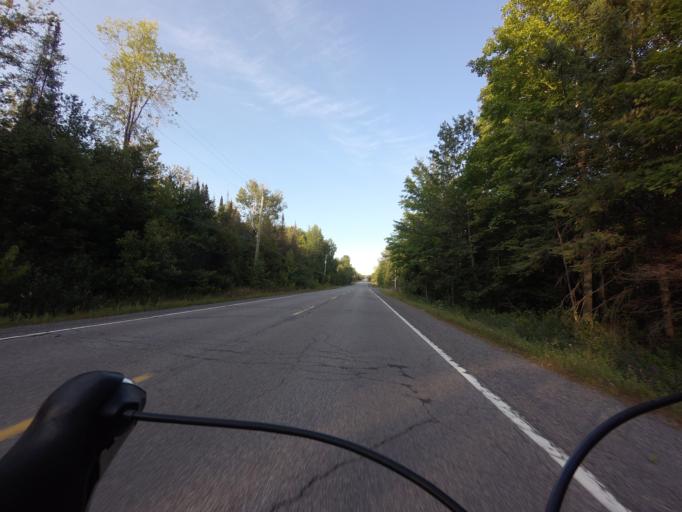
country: CA
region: Ontario
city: Bells Corners
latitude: 45.3835
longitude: -75.9466
